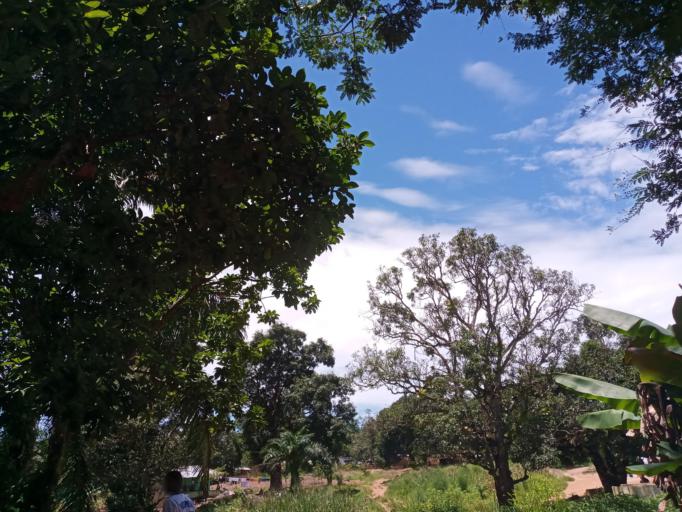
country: SL
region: Eastern Province
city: Koidu
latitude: 8.6523
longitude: -10.9616
